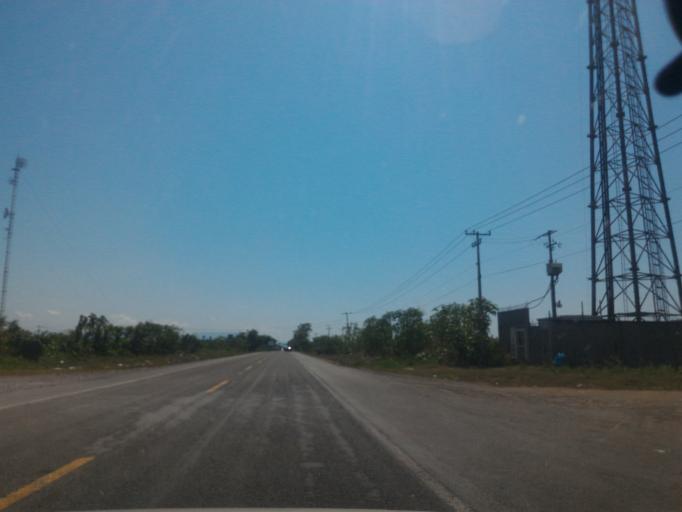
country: MX
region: Colima
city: Tecoman
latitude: 18.8272
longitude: -103.8139
